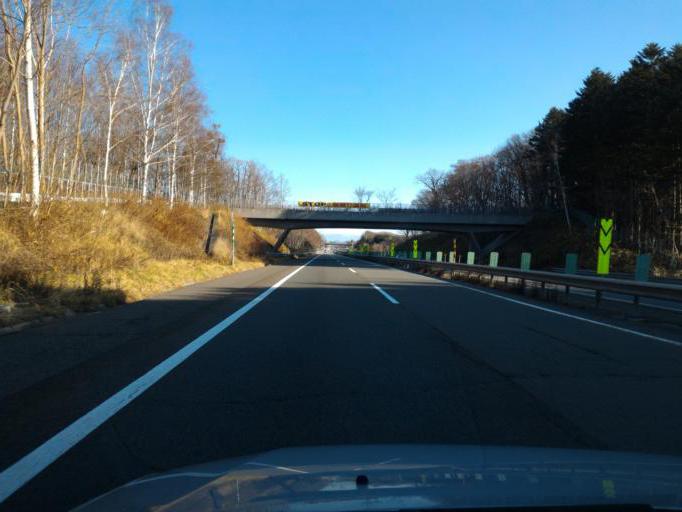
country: JP
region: Hokkaido
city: Iwamizawa
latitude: 43.1876
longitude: 141.7896
